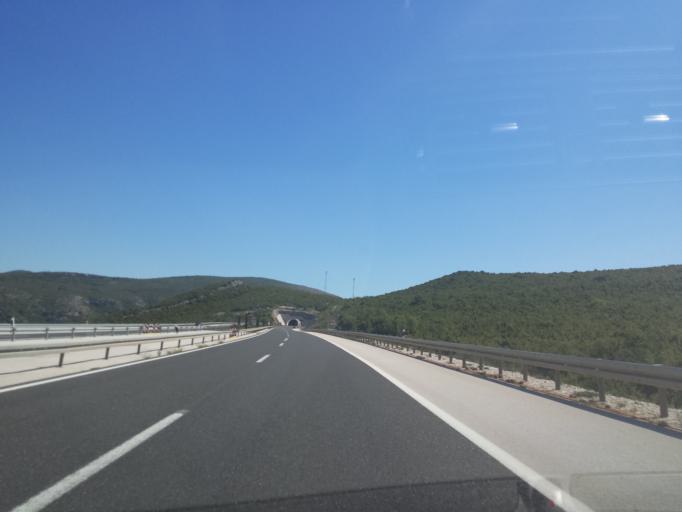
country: HR
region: Splitsko-Dalmatinska
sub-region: Grad Omis
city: Omis
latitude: 43.4788
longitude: 16.8154
